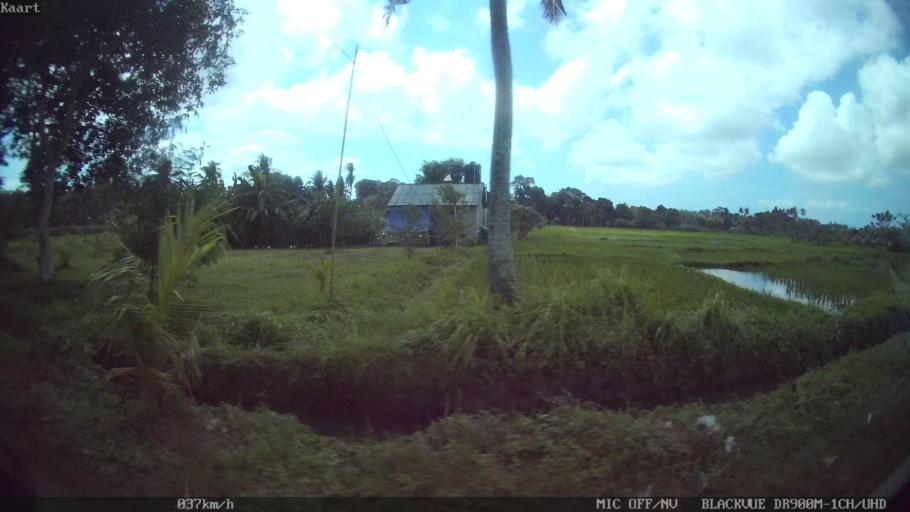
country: ID
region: Bali
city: Banjar Sedang
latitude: -8.5694
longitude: 115.2861
